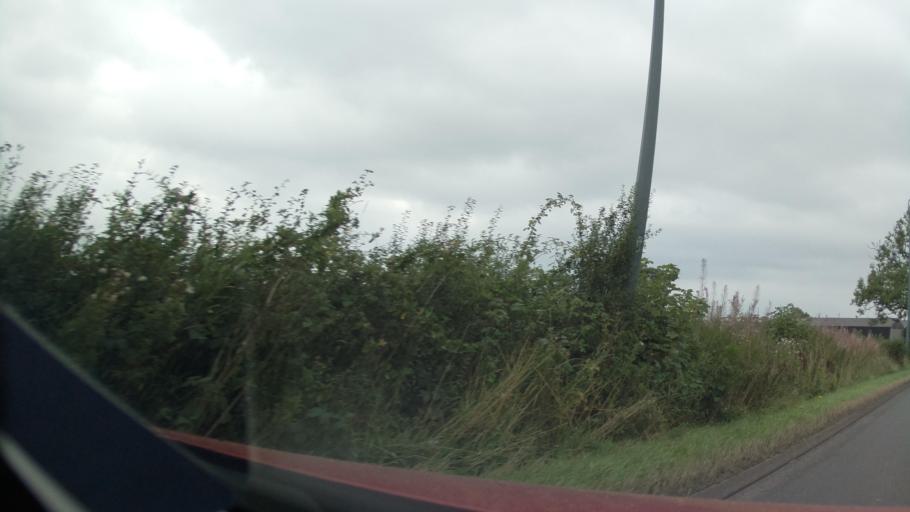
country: GB
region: England
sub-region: Staffordshire
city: Cheadle
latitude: 53.0164
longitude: -2.0237
